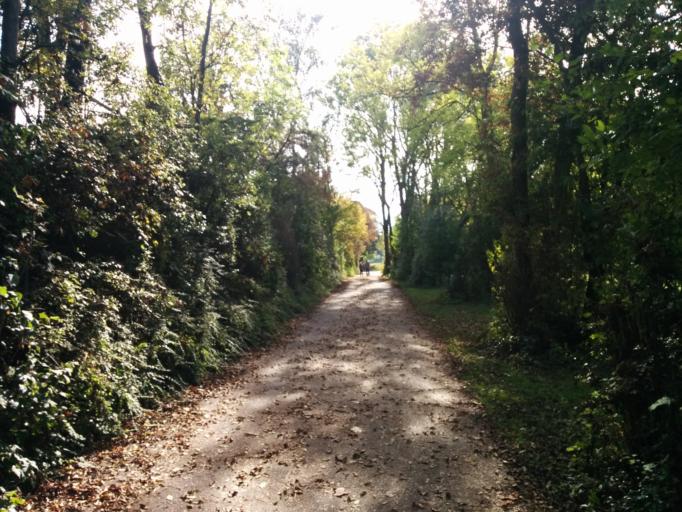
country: DE
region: Bavaria
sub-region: Upper Bavaria
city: Oberschleissheim
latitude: 48.2071
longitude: 11.5292
